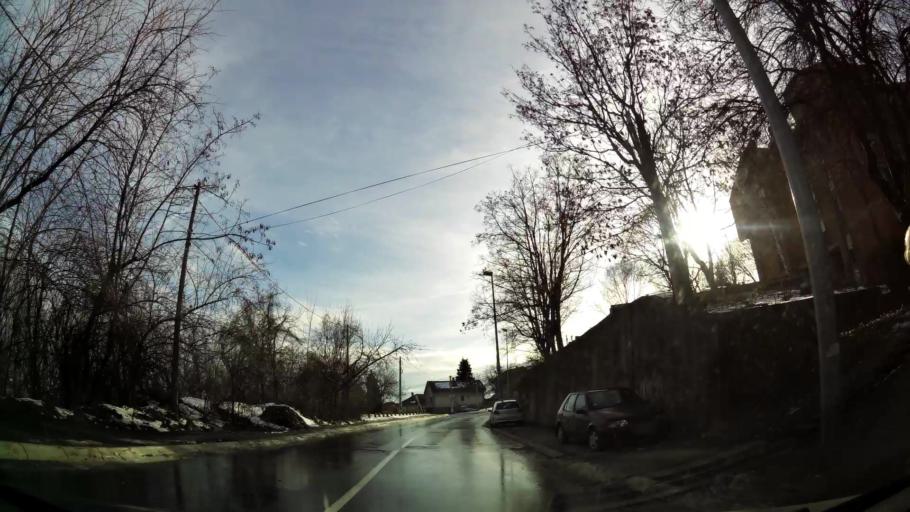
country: RS
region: Central Serbia
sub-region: Belgrade
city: Rakovica
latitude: 44.7264
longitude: 20.4318
